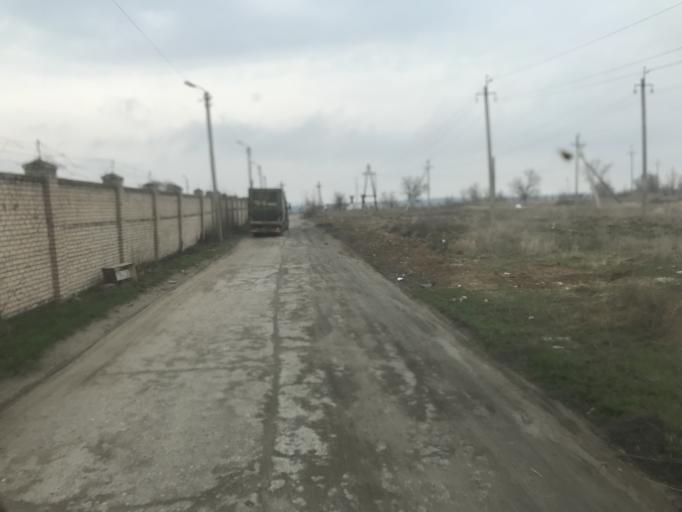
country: RU
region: Volgograd
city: Krasnoslobodsk
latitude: 48.5351
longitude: 44.5833
